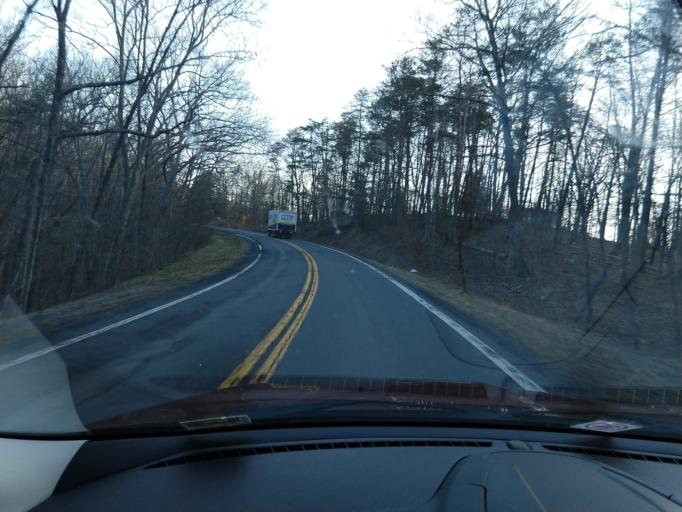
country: US
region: Virginia
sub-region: Frederick County
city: Shawnee Land
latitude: 39.4041
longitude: -78.4404
